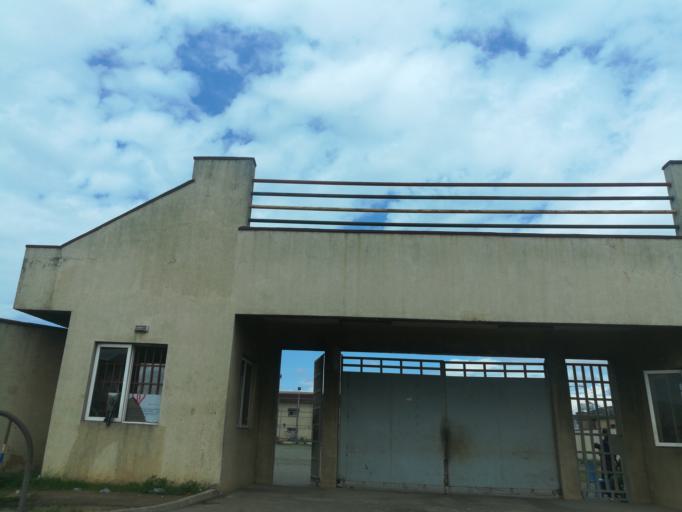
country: NG
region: Lagos
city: Agege
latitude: 6.6229
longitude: 3.3293
